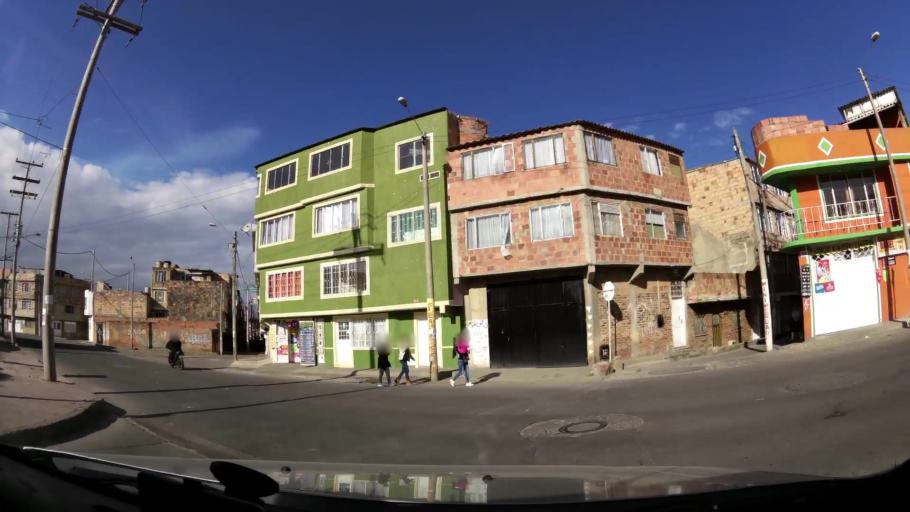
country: CO
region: Cundinamarca
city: Soacha
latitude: 4.5683
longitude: -74.1512
